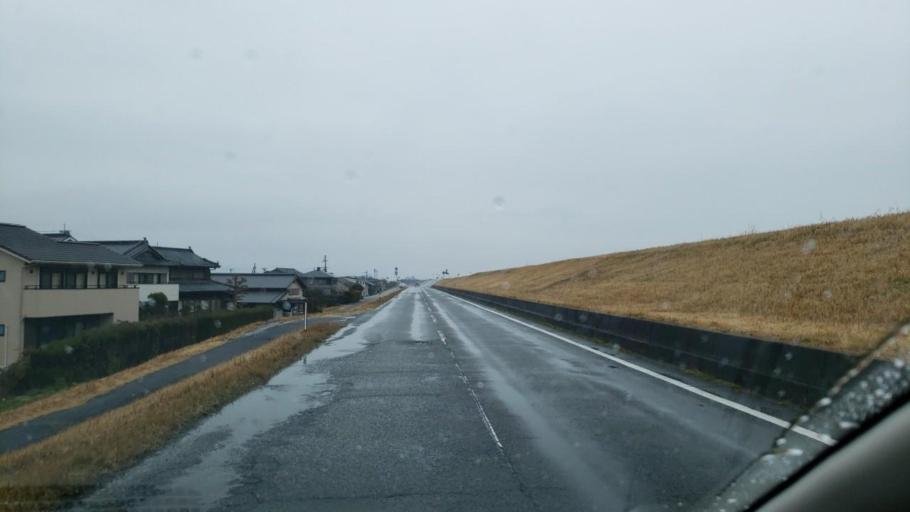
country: JP
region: Tokushima
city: Ishii
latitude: 34.1009
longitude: 134.4159
